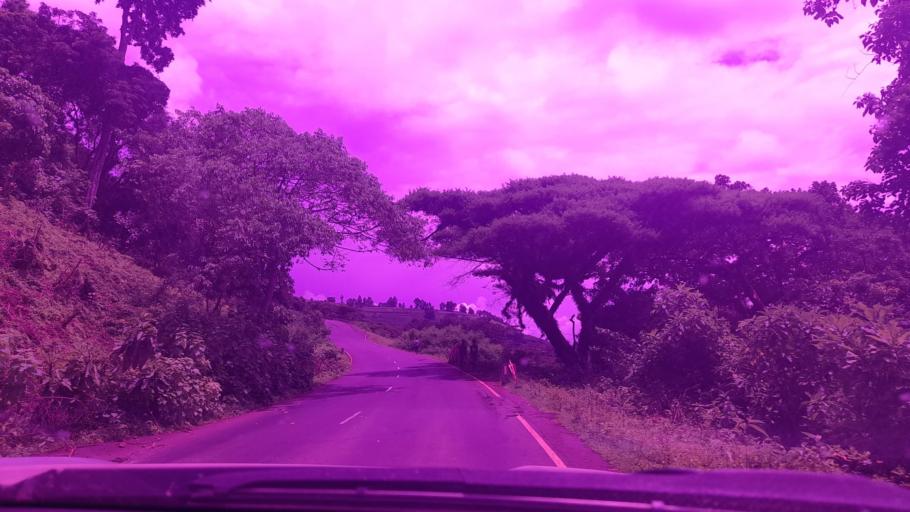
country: ET
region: Oromiya
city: Metu
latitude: 8.3362
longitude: 35.7460
